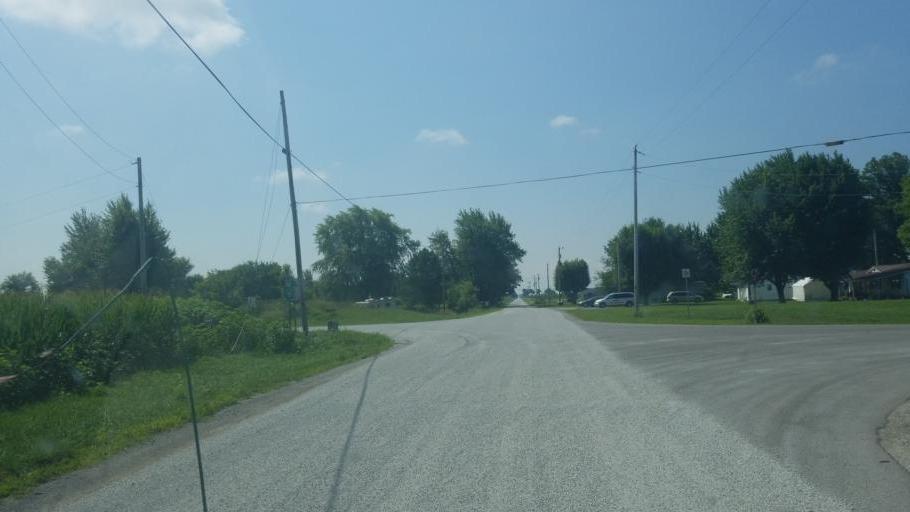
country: US
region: Ohio
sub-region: Hardin County
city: Kenton
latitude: 40.6769
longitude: -83.7292
